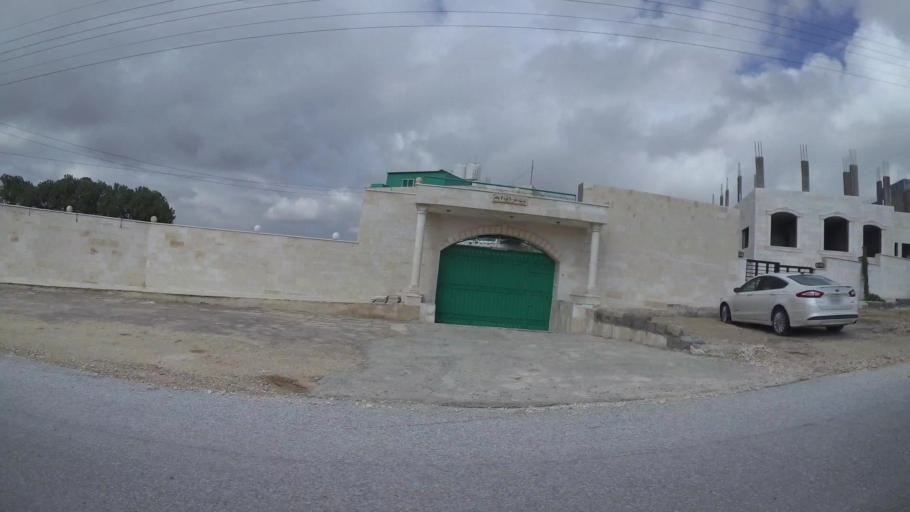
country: JO
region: Amman
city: Al Jubayhah
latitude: 32.0711
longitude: 35.8663
